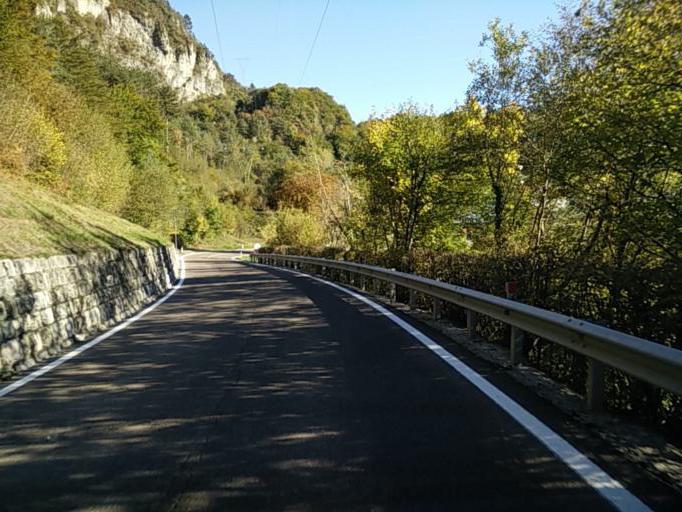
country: IT
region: Trentino-Alto Adige
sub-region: Provincia di Trento
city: Molina di Ledro
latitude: 45.8785
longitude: 10.7672
